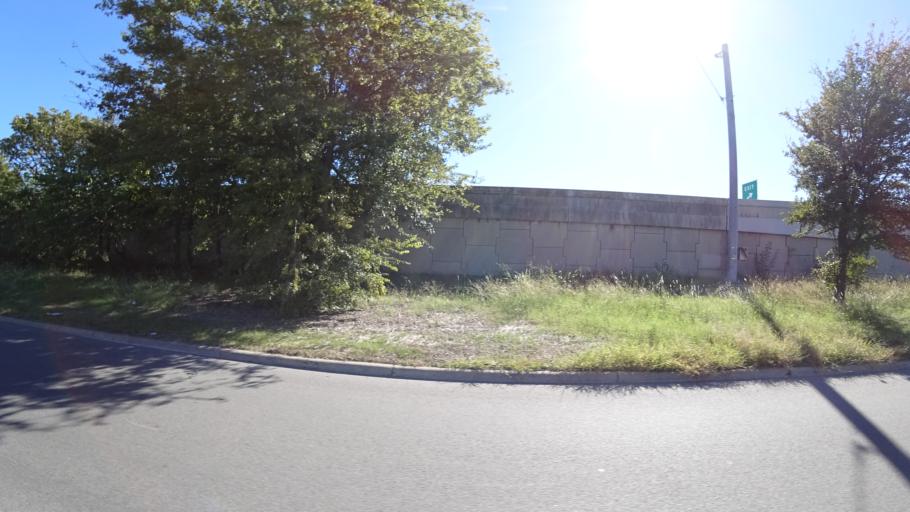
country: US
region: Texas
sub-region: Travis County
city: Rollingwood
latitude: 30.2338
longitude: -97.8195
